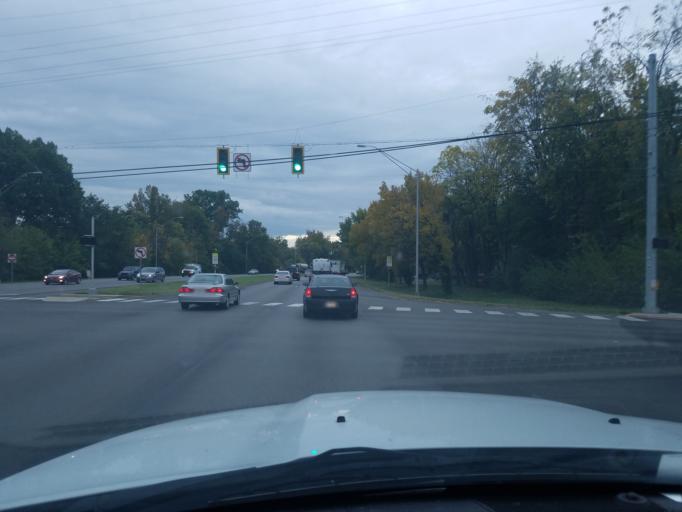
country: US
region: Indiana
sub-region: Vanderburgh County
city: Evansville
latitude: 37.9683
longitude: -87.5433
